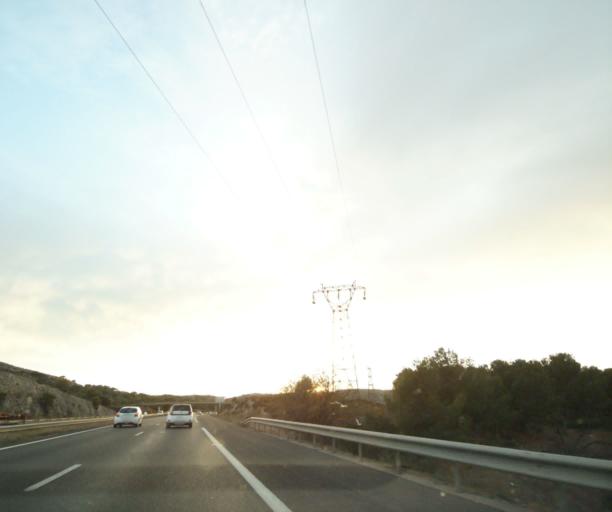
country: FR
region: Provence-Alpes-Cote d'Azur
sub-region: Departement des Bouches-du-Rhone
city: Ensues-la-Redonne
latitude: 43.3769
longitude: 5.2015
